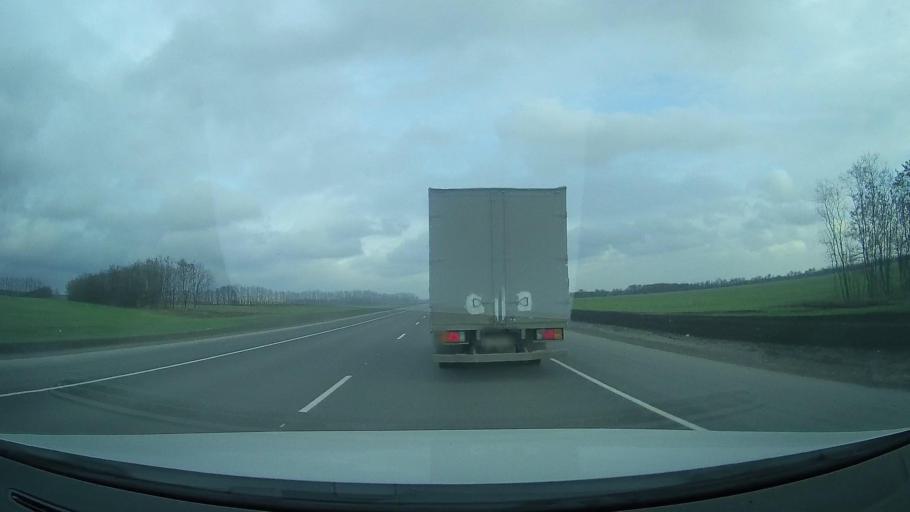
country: RU
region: Rostov
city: Grushevskaya
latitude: 47.4703
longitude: 39.9030
